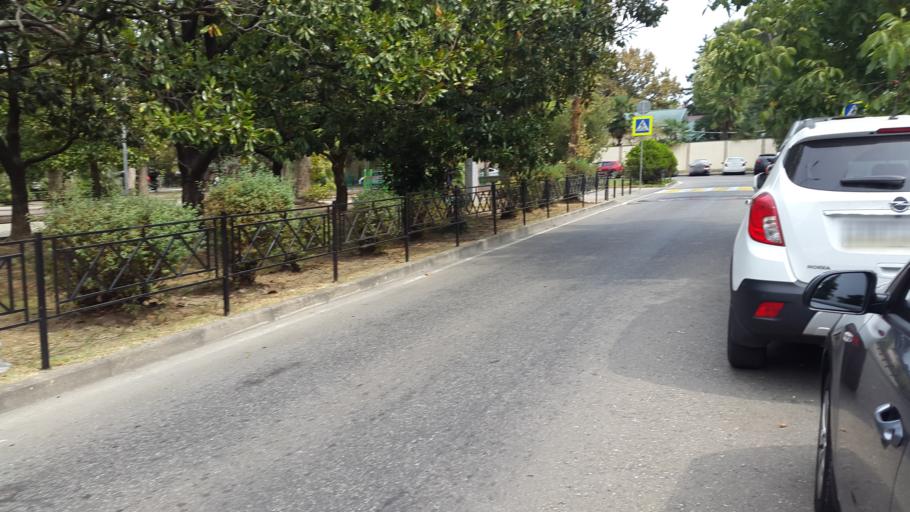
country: RU
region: Krasnodarskiy
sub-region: Sochi City
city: Sochi
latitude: 43.6013
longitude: 39.7246
